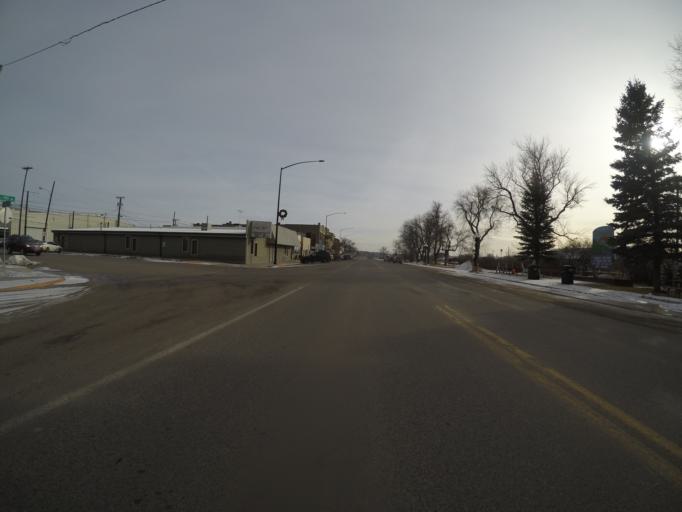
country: US
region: Montana
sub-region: Stillwater County
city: Columbus
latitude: 45.6372
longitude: -109.2540
